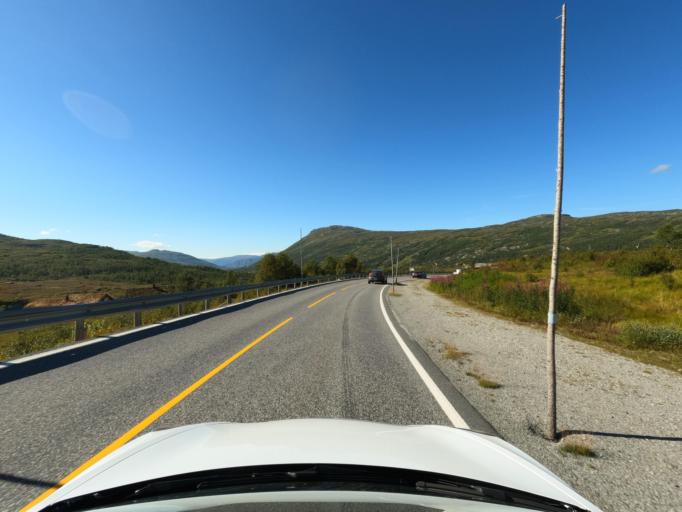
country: NO
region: Hordaland
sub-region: Eidfjord
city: Eidfjord
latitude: 60.4036
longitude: 7.3612
